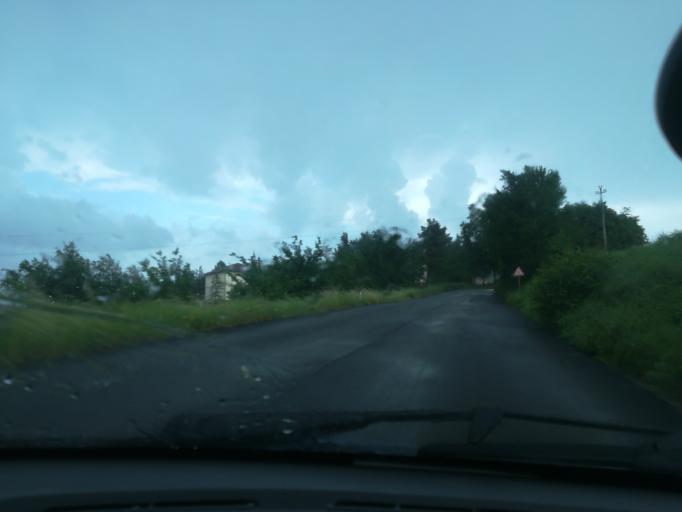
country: IT
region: The Marches
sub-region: Provincia di Macerata
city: Casette Verdini
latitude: 43.2874
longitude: 13.3900
